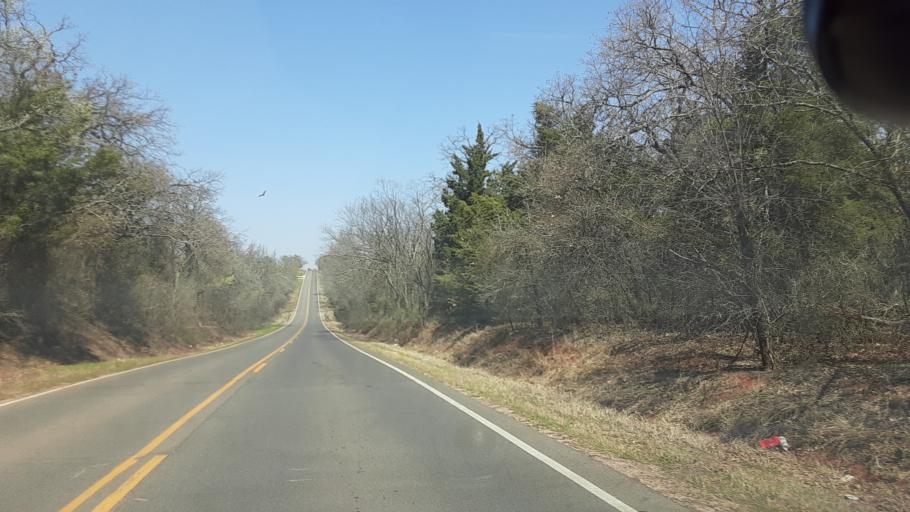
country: US
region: Oklahoma
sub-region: Oklahoma County
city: Edmond
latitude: 35.7690
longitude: -97.4784
